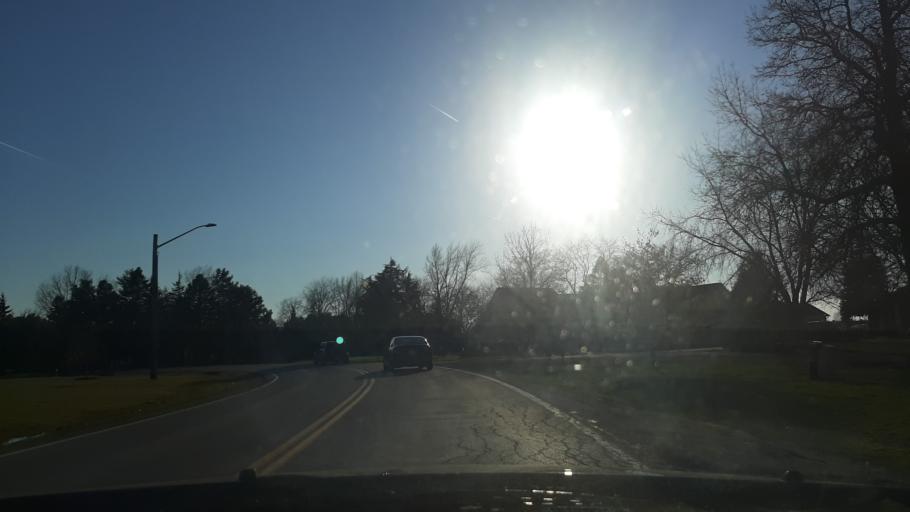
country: US
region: New York
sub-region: Niagara County
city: Lewiston
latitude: 43.1694
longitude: -79.0601
